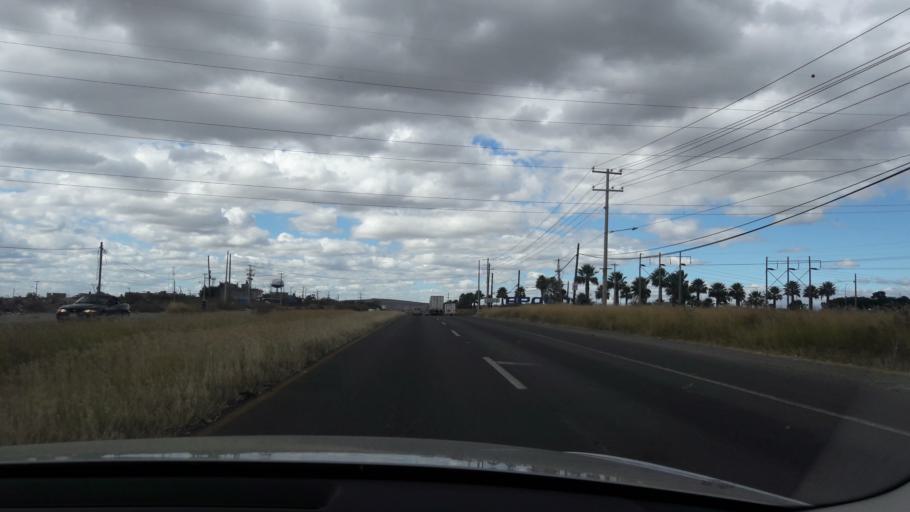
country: MX
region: Guanajuato
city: San Jose Temascatio
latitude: 20.6872
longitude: -101.3070
